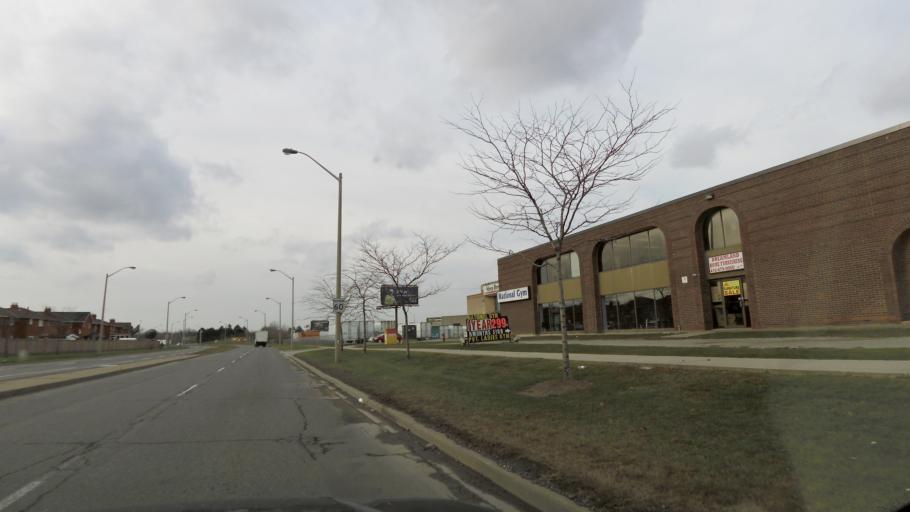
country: CA
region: Ontario
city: Etobicoke
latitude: 43.7351
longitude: -79.6182
